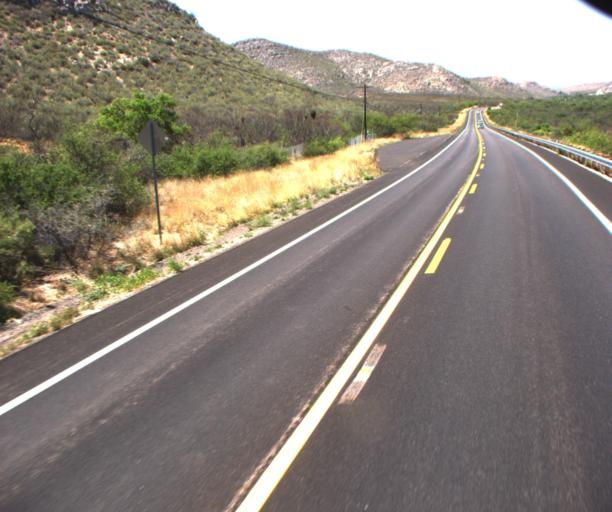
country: US
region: Arizona
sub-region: Cochise County
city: Bisbee
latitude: 31.5063
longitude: -110.0096
